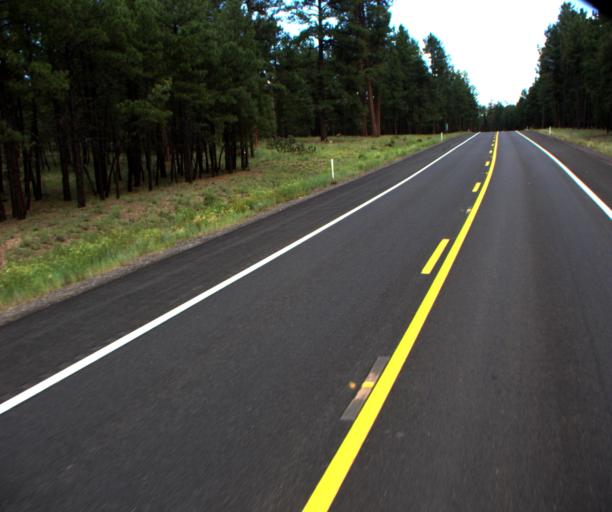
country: US
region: Arizona
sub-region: Coconino County
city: Flagstaff
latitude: 35.2549
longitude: -111.7013
